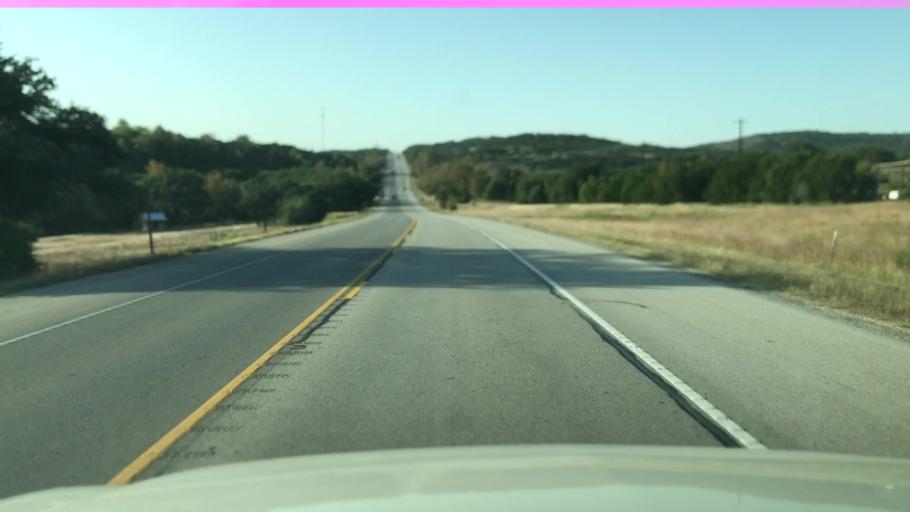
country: US
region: Texas
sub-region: Blanco County
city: Johnson City
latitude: 30.1885
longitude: -98.3781
